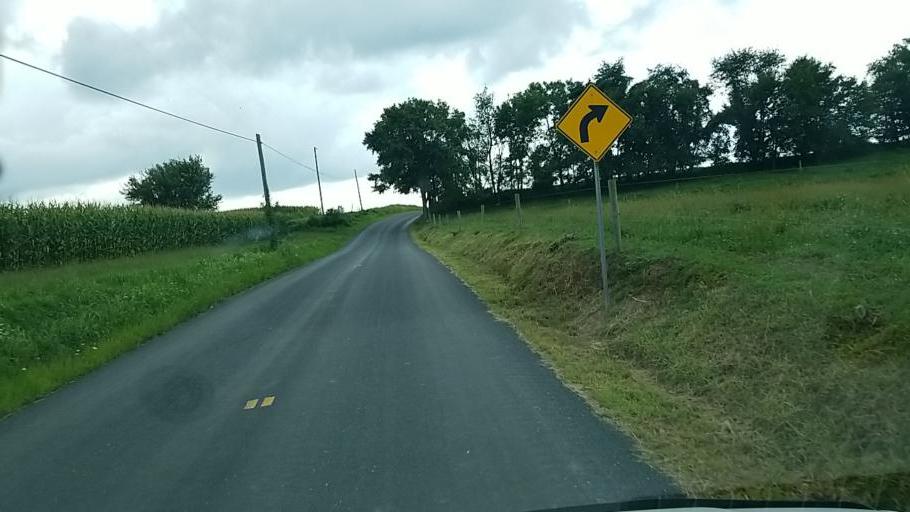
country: US
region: Pennsylvania
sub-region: Dauphin County
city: Elizabethville
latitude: 40.5750
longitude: -76.8479
